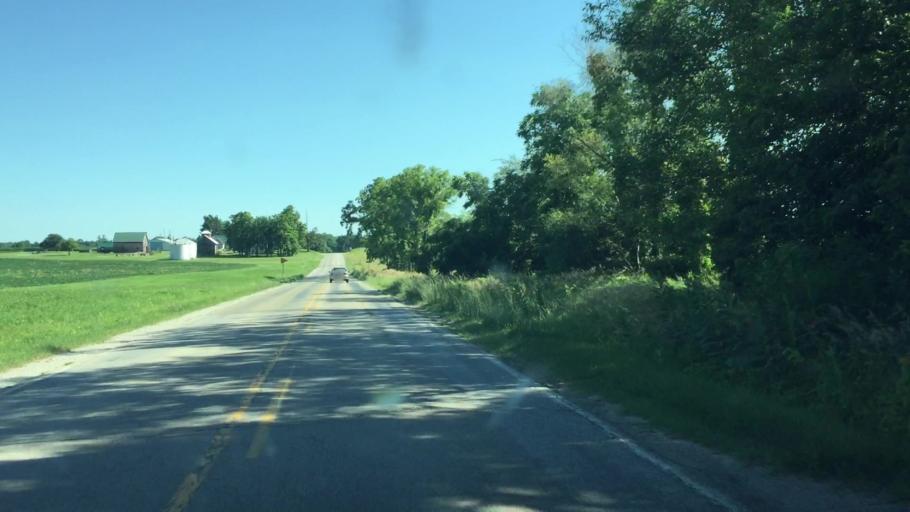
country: US
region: Iowa
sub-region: Linn County
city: Ely
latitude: 41.8594
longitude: -91.6464
